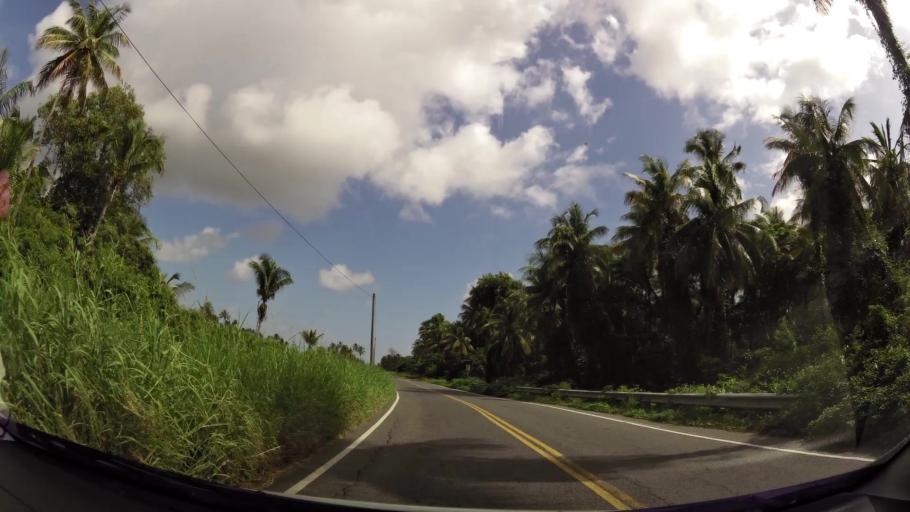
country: GY
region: Demerara-Mahaica
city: Mahaica Village
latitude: 6.7200
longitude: -57.9344
